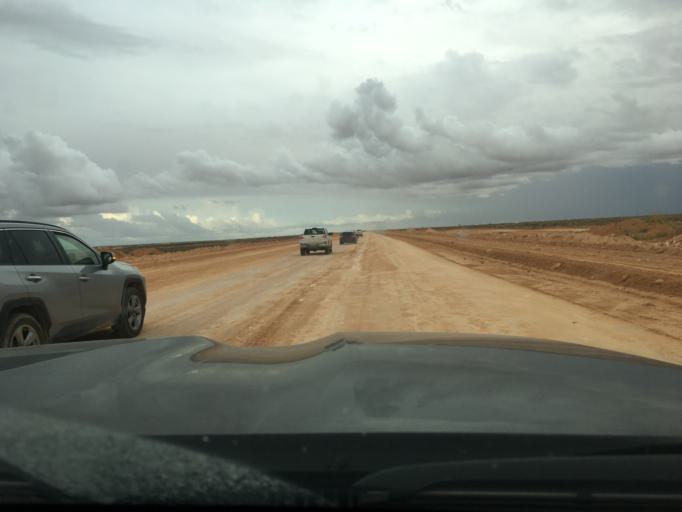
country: TN
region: Madanin
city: Medenine
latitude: 33.2726
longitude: 10.5885
